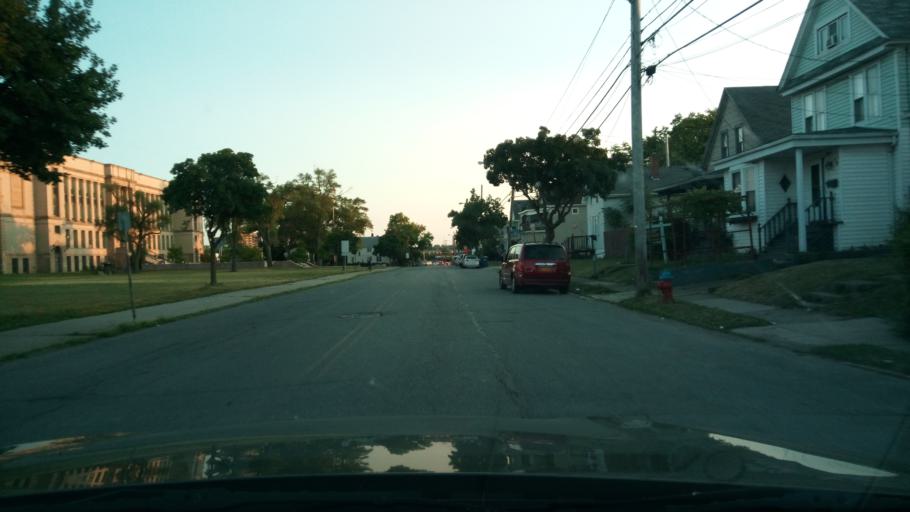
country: US
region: New York
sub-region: Erie County
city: Kenmore
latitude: 42.9479
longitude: -78.9055
